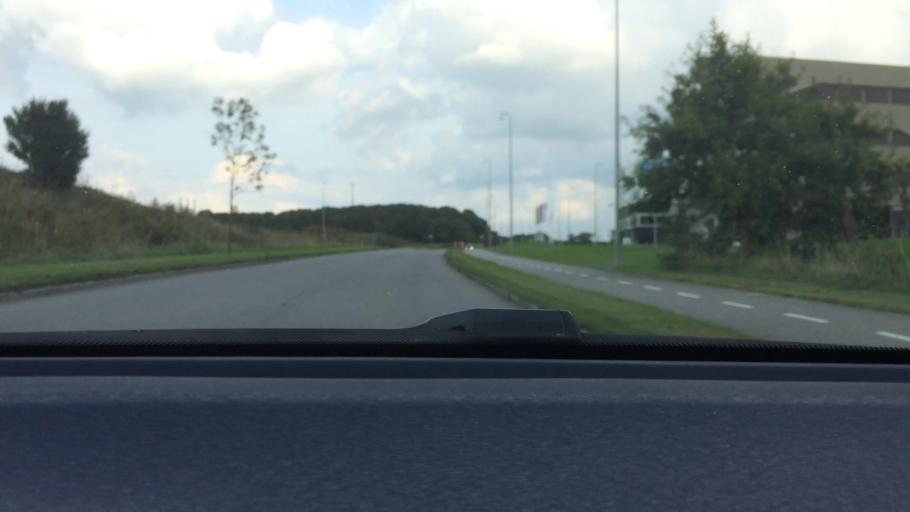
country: DK
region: South Denmark
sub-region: Vejle Kommune
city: Vejle
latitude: 55.7345
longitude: 9.5793
